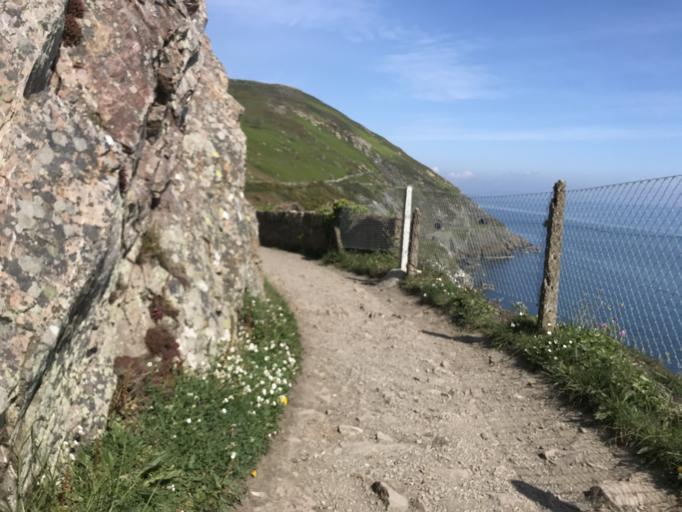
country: IE
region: Leinster
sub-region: Wicklow
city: Bray
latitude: 53.1826
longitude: -6.0765
